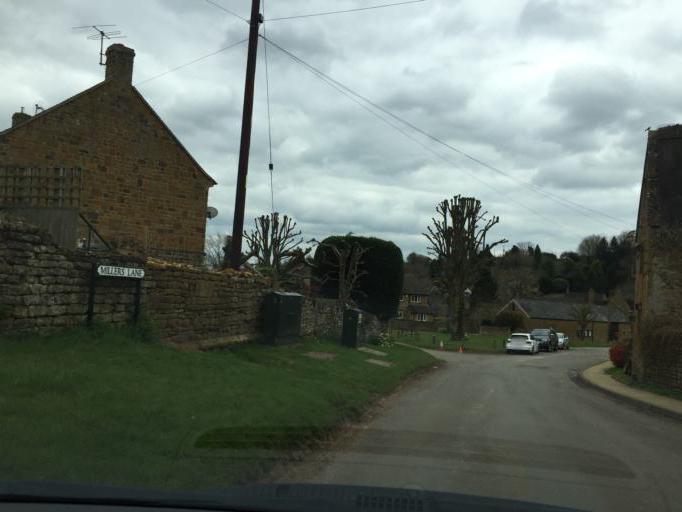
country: GB
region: England
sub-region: Oxfordshire
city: Hanwell
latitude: 52.1024
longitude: -1.4274
